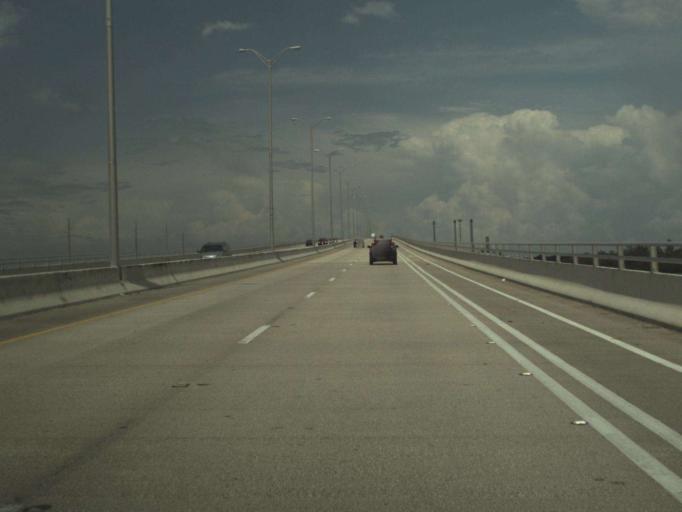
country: US
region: Florida
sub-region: Indian River County
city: Vero Beach
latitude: 27.6323
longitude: -80.3648
